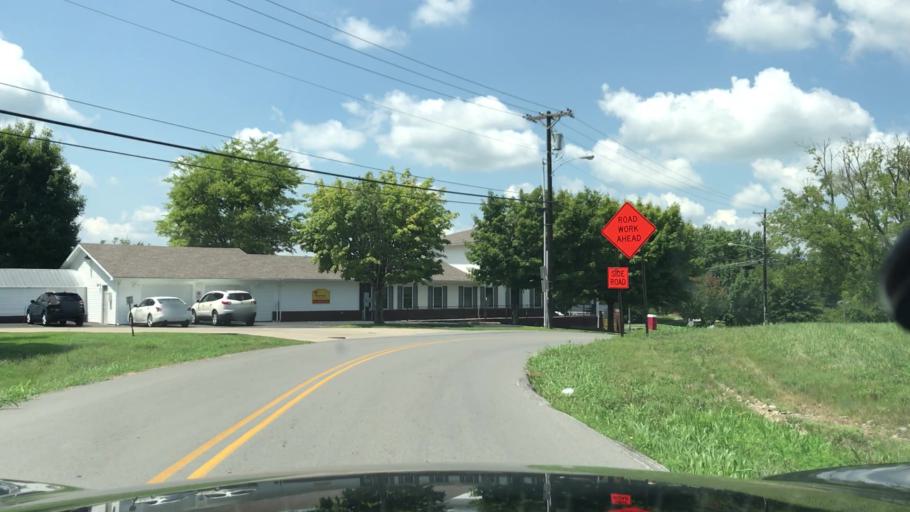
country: US
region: Kentucky
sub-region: Adair County
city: Columbia
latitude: 37.0971
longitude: -85.3134
